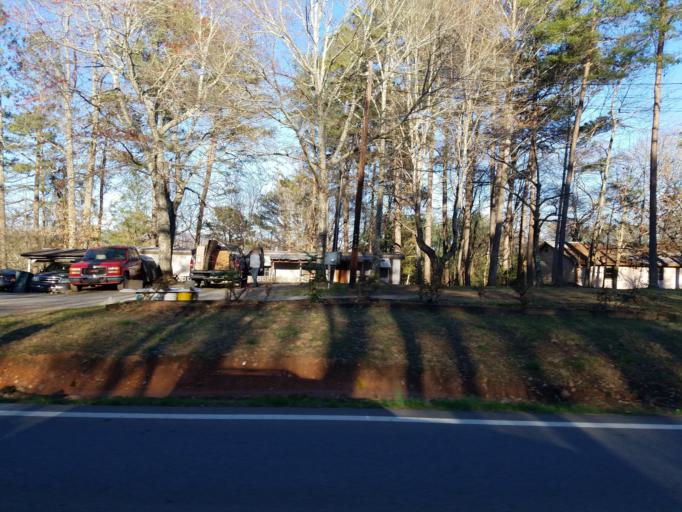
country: US
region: Georgia
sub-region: Pickens County
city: Jasper
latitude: 34.4332
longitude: -84.4213
